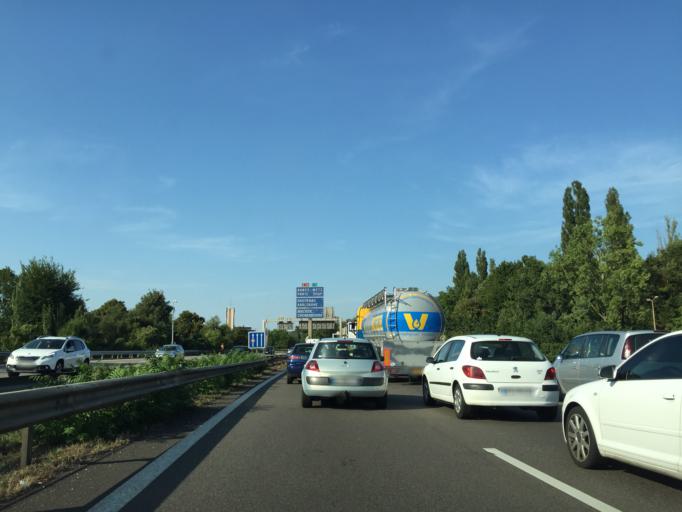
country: FR
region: Alsace
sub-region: Departement du Bas-Rhin
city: Strasbourg
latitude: 48.5848
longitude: 7.7248
